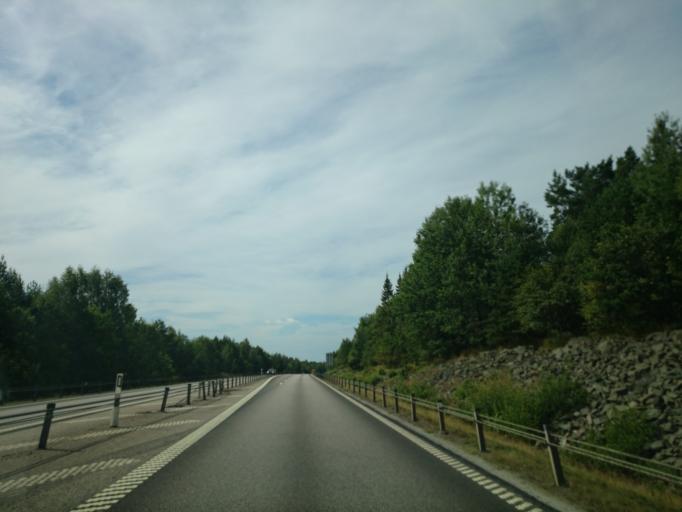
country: SE
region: Kalmar
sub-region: Oskarshamns Kommun
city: Oskarshamn
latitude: 57.2932
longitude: 16.4587
